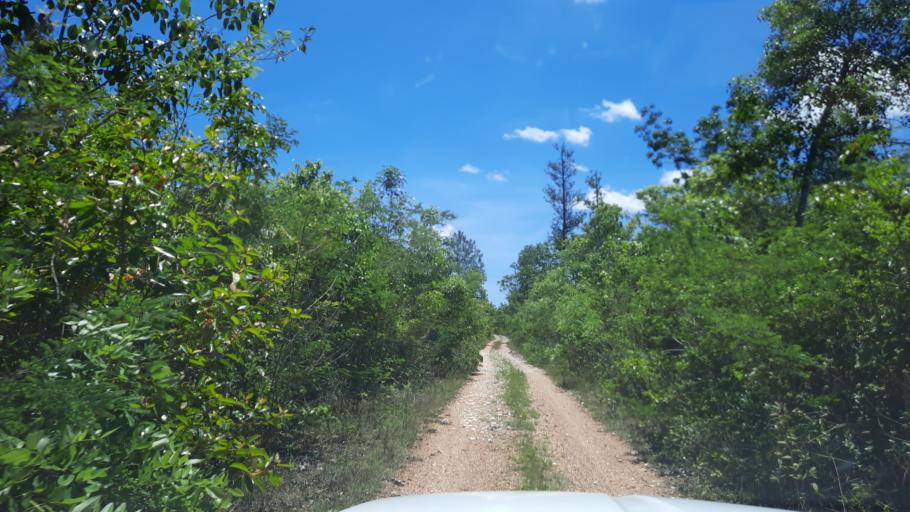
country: BZ
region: Cayo
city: Belmopan
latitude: 17.3588
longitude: -88.5349
